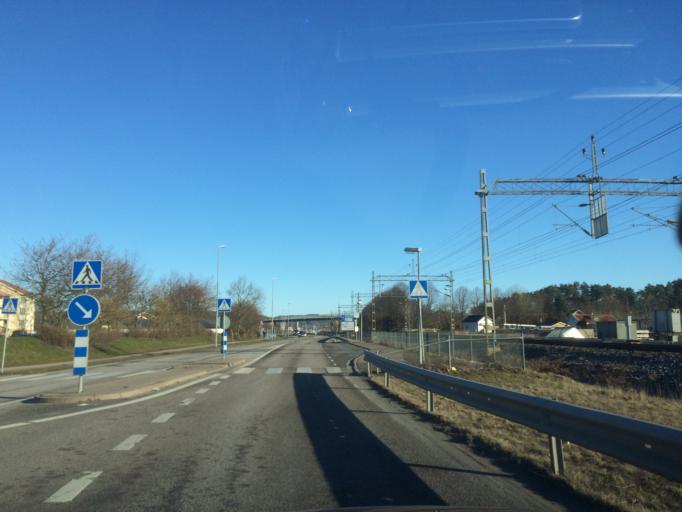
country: SE
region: Halland
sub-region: Kungsbacka Kommun
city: Kungsbacka
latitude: 57.4972
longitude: 12.0801
